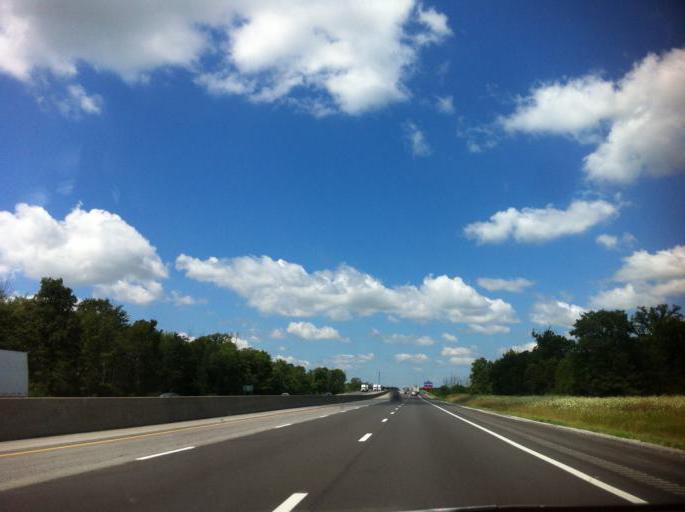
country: US
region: Ohio
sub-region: Sandusky County
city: Woodville
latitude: 41.4829
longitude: -83.3518
